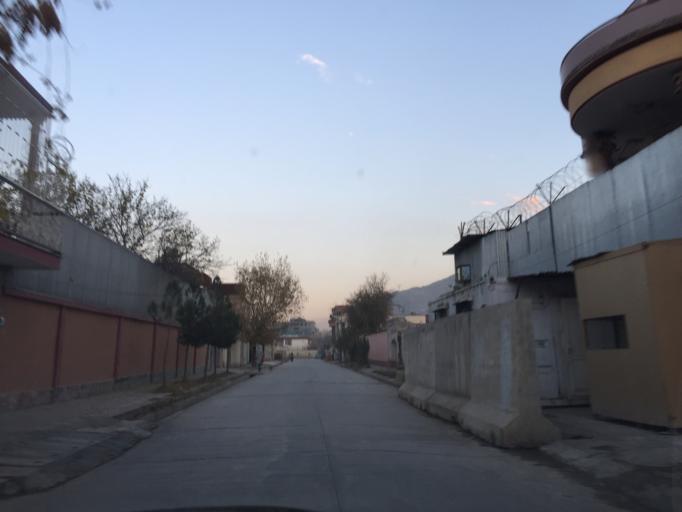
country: AF
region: Kabul
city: Kabul
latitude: 34.5072
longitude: 69.1383
